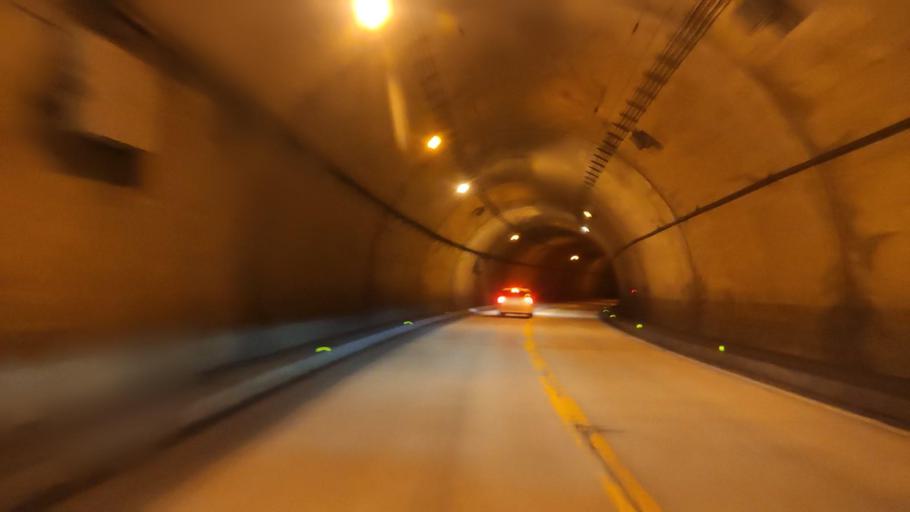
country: JP
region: Nara
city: Yoshino-cho
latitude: 34.2514
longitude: 135.9960
